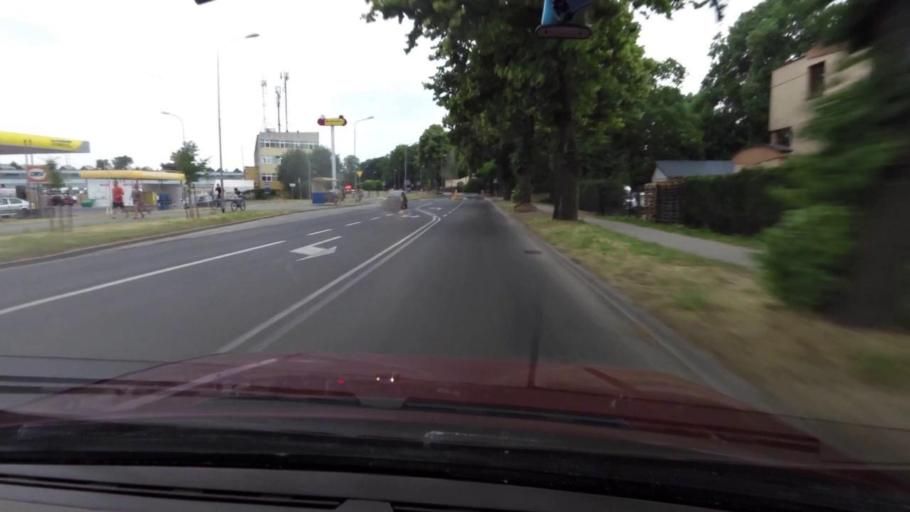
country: PL
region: West Pomeranian Voivodeship
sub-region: Koszalin
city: Koszalin
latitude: 54.1882
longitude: 16.2358
